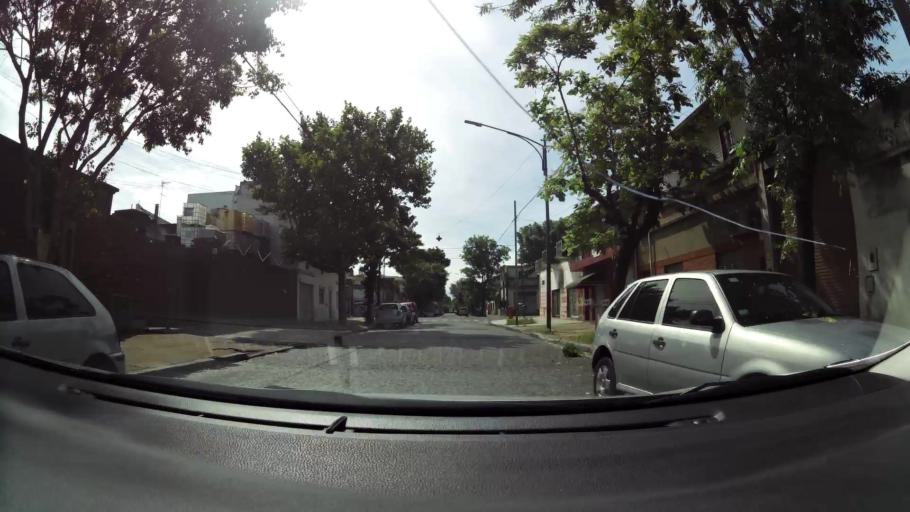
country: AR
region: Buenos Aires F.D.
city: Villa Lugano
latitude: -34.6556
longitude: -58.4279
